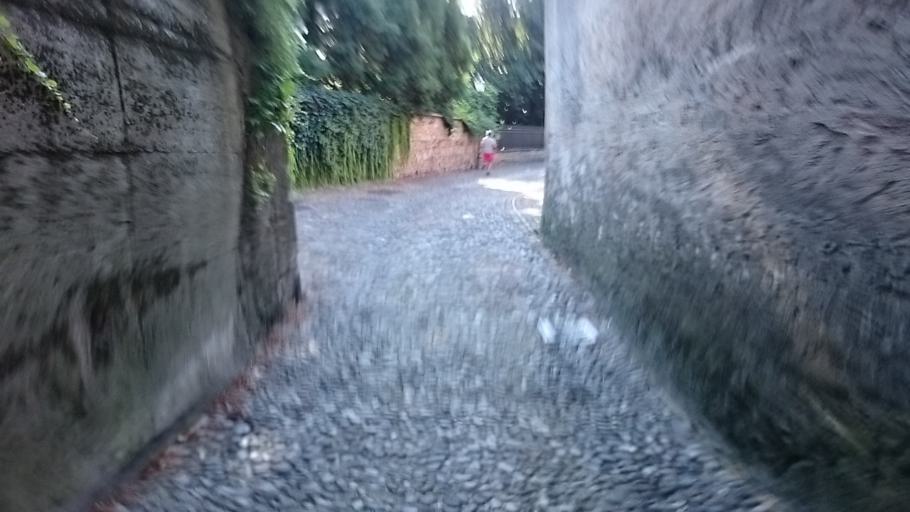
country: IT
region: Veneto
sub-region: Provincia di Vicenza
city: Vicenza
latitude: 45.5381
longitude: 11.5525
